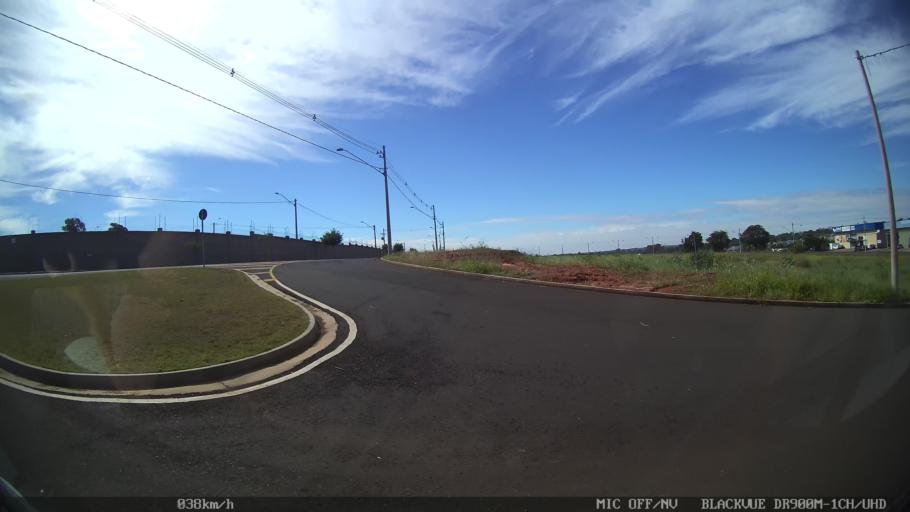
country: BR
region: Sao Paulo
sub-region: Sao Jose Do Rio Preto
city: Sao Jose do Rio Preto
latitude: -20.8555
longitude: -49.3724
